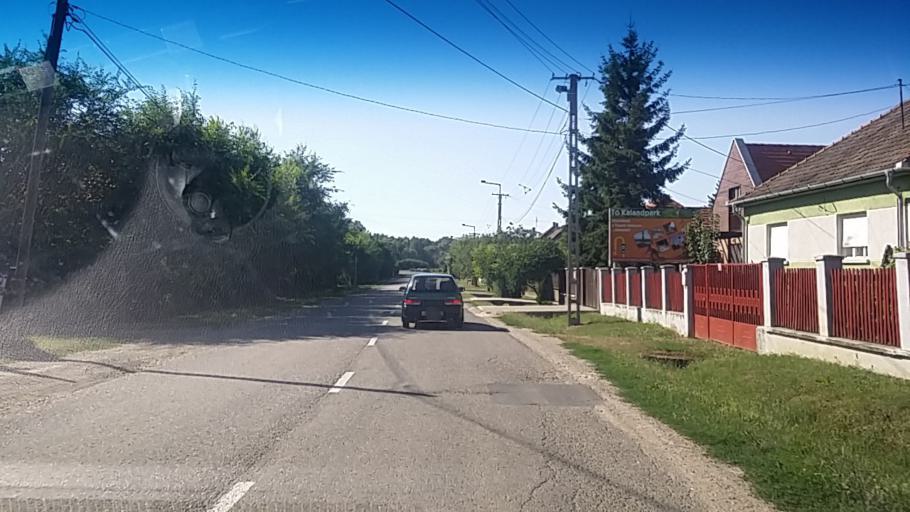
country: HU
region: Nograd
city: Retsag
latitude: 47.9295
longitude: 19.1706
